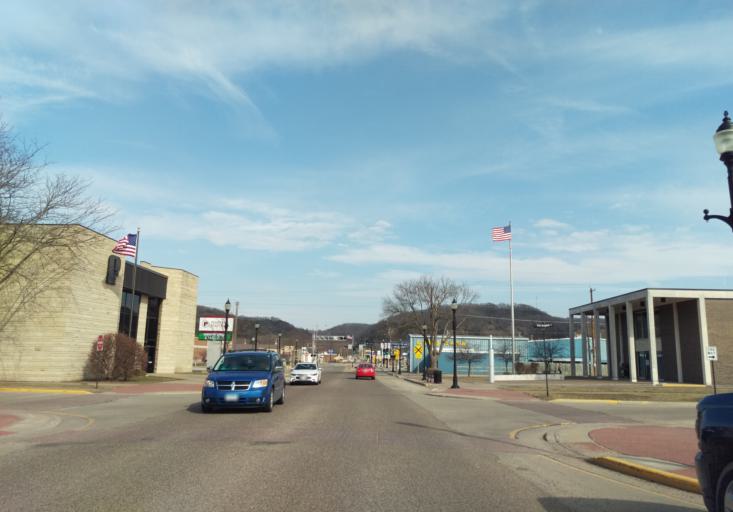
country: US
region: Wisconsin
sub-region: Crawford County
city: Prairie du Chien
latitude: 43.0518
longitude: -91.1441
